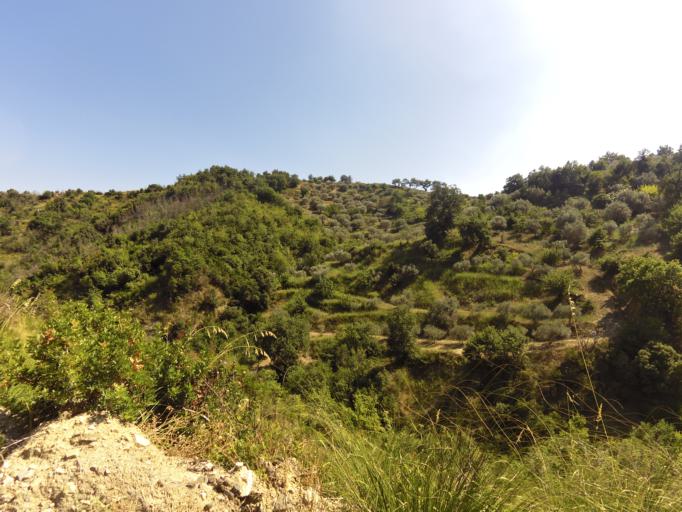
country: IT
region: Calabria
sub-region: Provincia di Reggio Calabria
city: Pazzano
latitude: 38.4633
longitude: 16.4552
